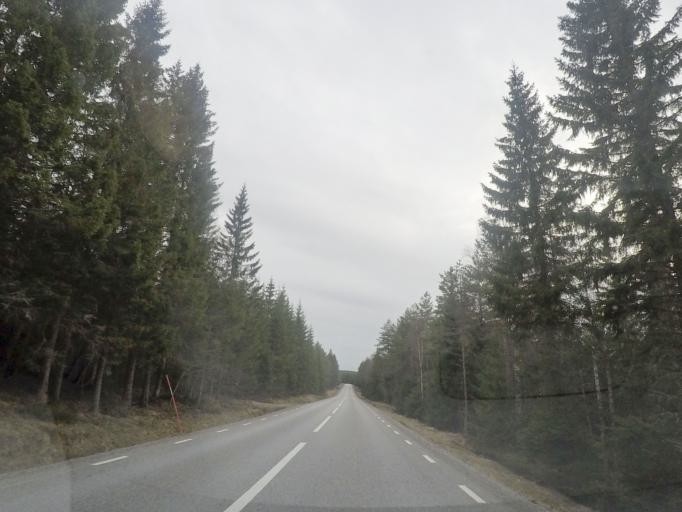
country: SE
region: OErebro
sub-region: Lindesbergs Kommun
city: Stora
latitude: 59.9004
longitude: 15.1933
